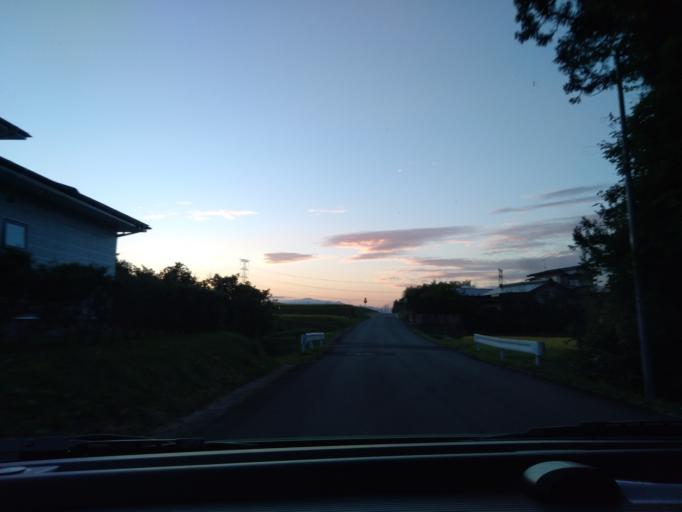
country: JP
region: Iwate
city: Ichinoseki
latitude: 38.8563
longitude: 141.1472
